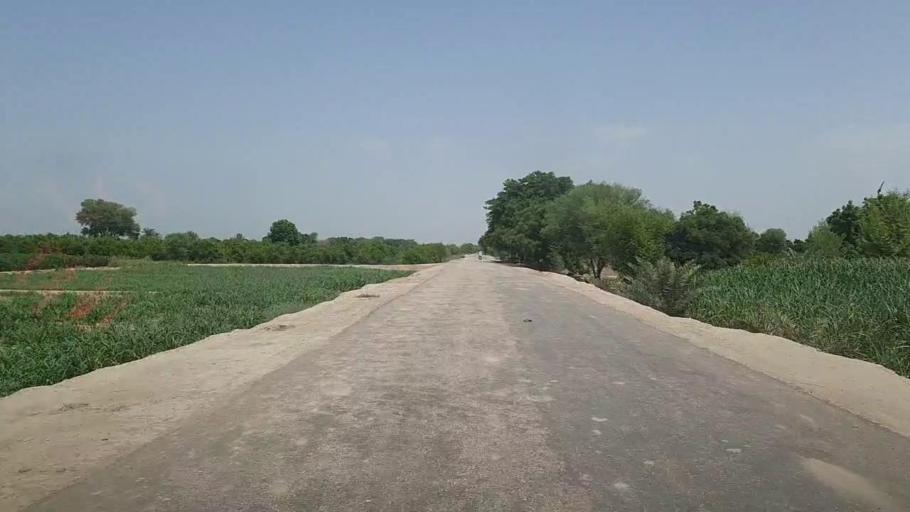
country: PK
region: Sindh
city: Pad Idan
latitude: 26.8430
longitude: 68.3379
